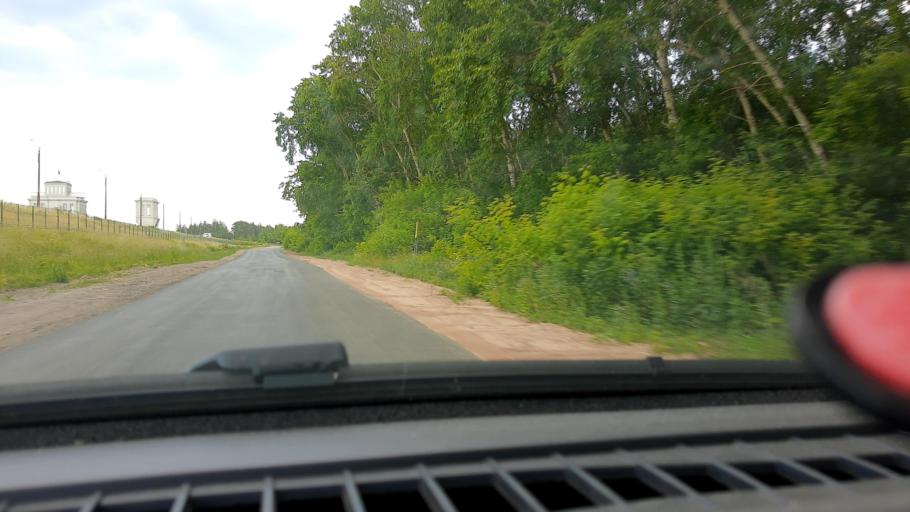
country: RU
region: Nizjnij Novgorod
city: Gorodets
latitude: 56.6657
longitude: 43.4325
